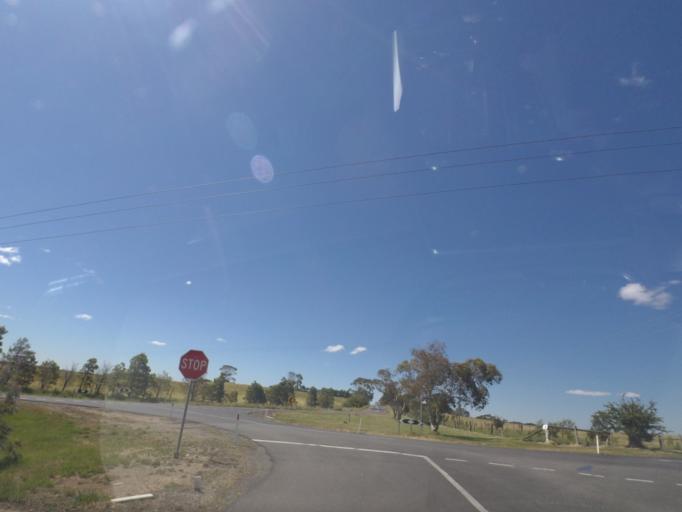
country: AU
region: Victoria
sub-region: Mount Alexander
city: Castlemaine
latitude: -37.2866
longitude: 144.4465
